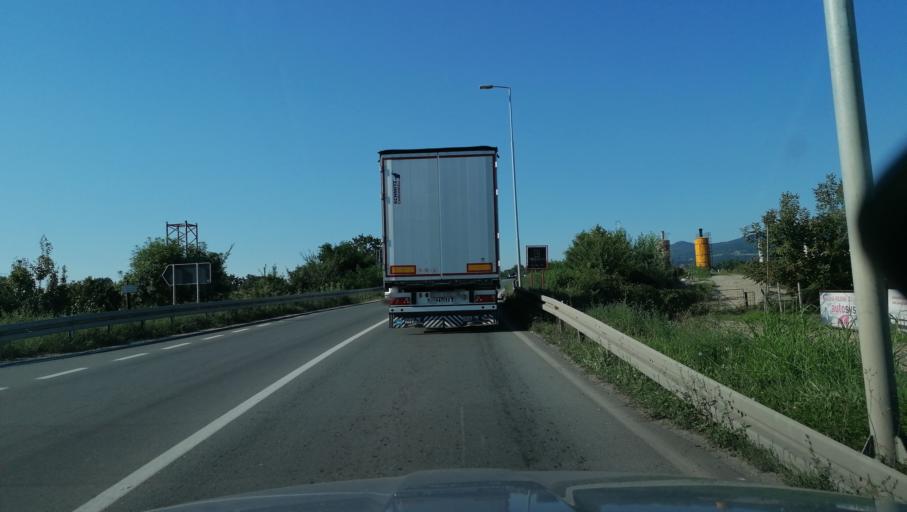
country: RS
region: Central Serbia
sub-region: Raski Okrug
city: Kraljevo
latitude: 43.7434
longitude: 20.6640
